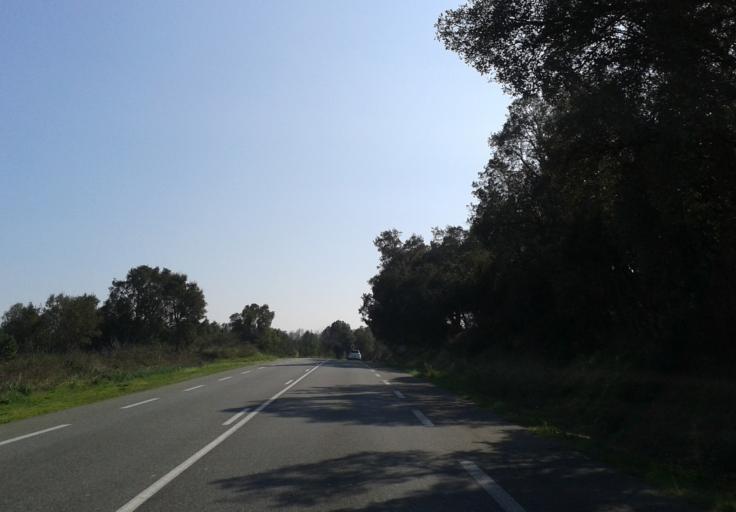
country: FR
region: Corsica
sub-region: Departement de la Haute-Corse
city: Linguizzetta
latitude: 42.2369
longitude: 9.5456
